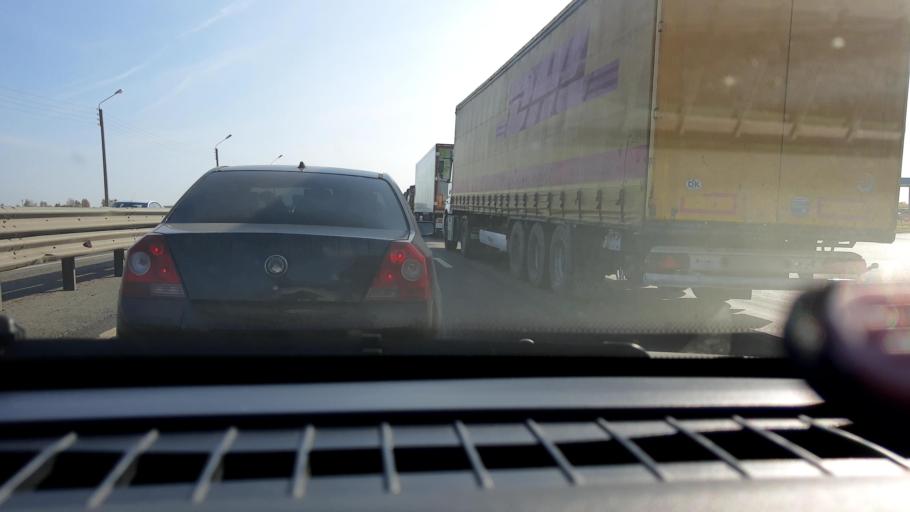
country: RU
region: Nizjnij Novgorod
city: Kstovo
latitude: 56.1249
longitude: 44.2662
